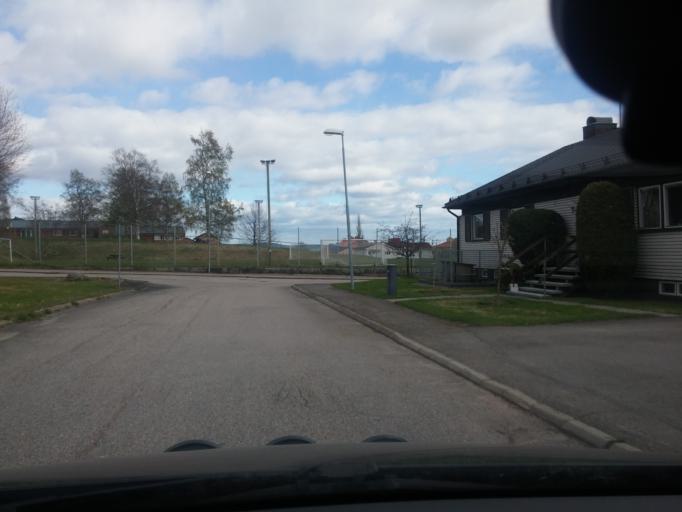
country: SE
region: Gaevleborg
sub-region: Ljusdals Kommun
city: Ljusdal
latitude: 61.8321
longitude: 16.0818
